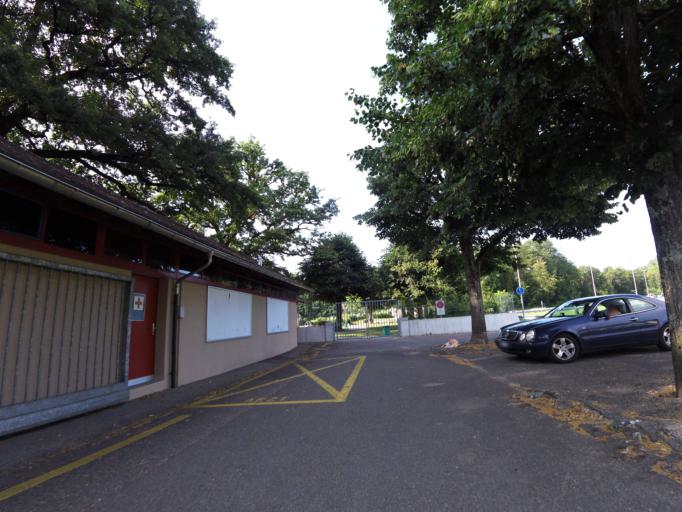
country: CH
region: Solothurn
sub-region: Bezirk Olten
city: Schonenwerd
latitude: 47.3789
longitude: 8.0021
